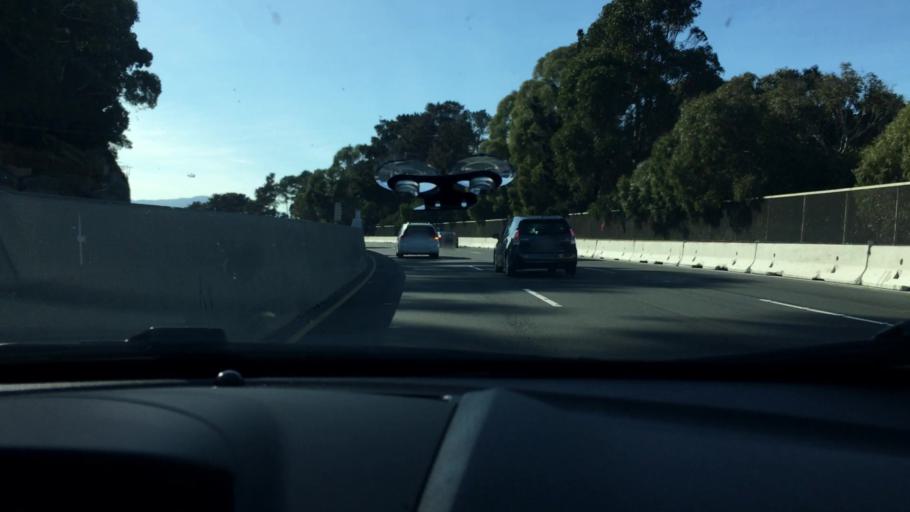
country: US
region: California
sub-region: Contra Costa County
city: North Richmond
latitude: 37.9326
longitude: -122.3951
